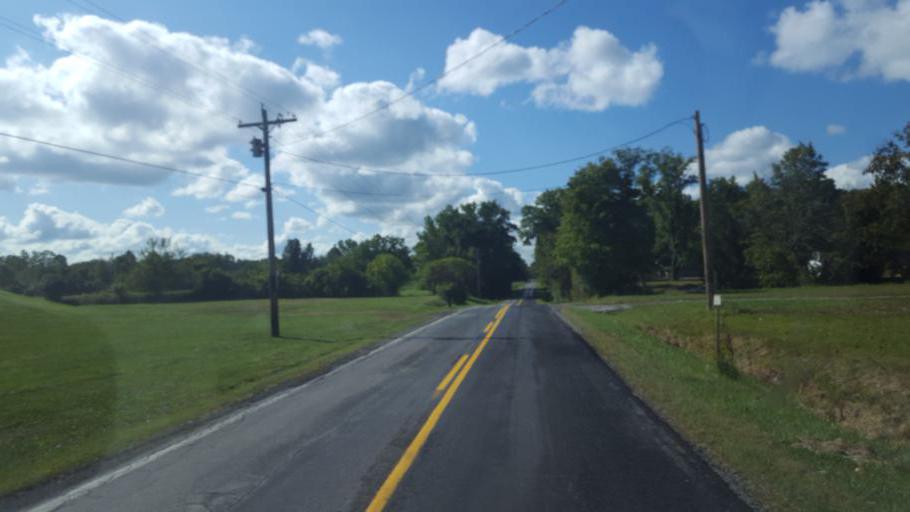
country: US
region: Ohio
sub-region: Lorain County
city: Oberlin
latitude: 41.2753
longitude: -82.1790
